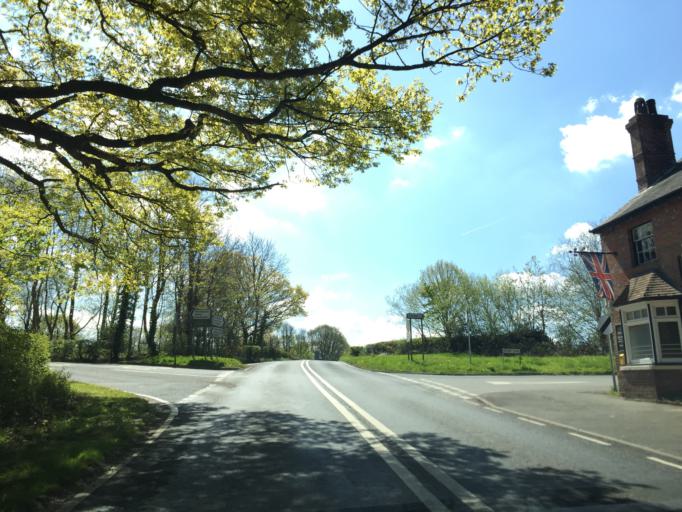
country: GB
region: England
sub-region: Kent
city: Edenbridge
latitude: 51.1637
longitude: 0.0911
